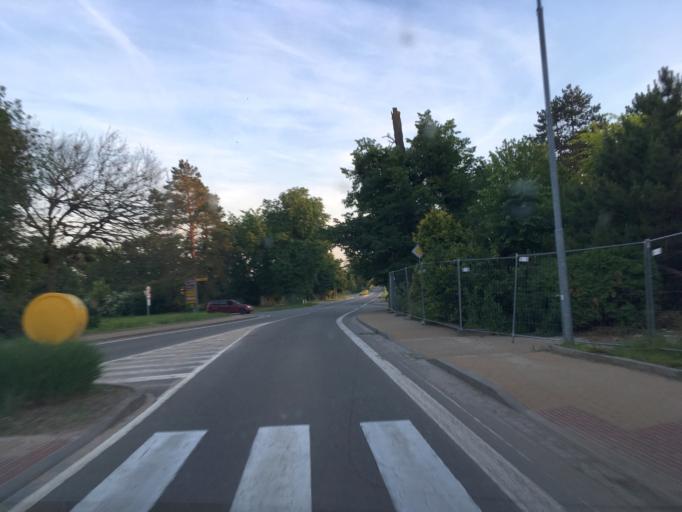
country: CZ
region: South Moravian
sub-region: Okres Breclav
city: Lednice
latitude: 48.7958
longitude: 16.8000
